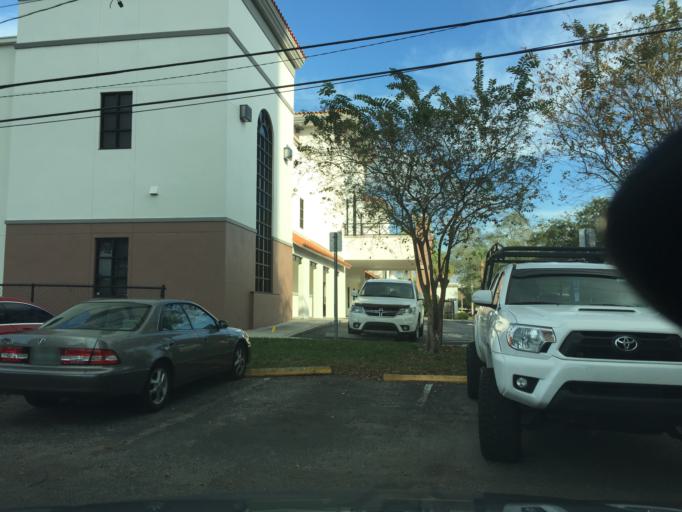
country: US
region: Florida
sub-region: Hillsborough County
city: Tampa
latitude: 27.9393
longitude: -82.4913
